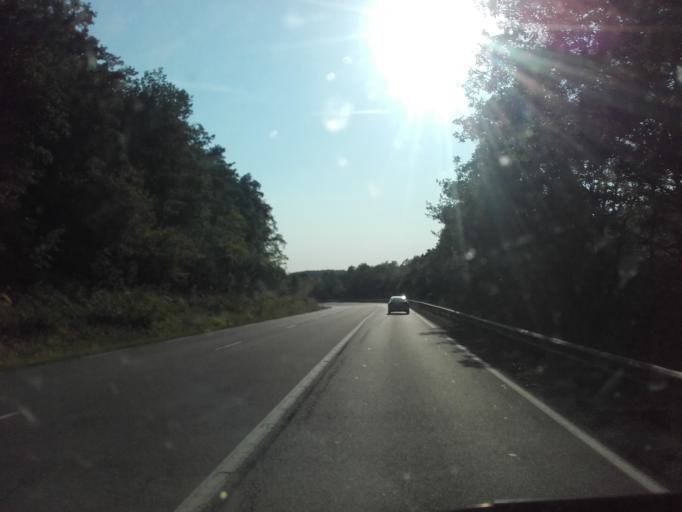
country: FR
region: Bourgogne
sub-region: Departement de l'Yonne
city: Venoy
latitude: 47.8069
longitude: 3.6730
